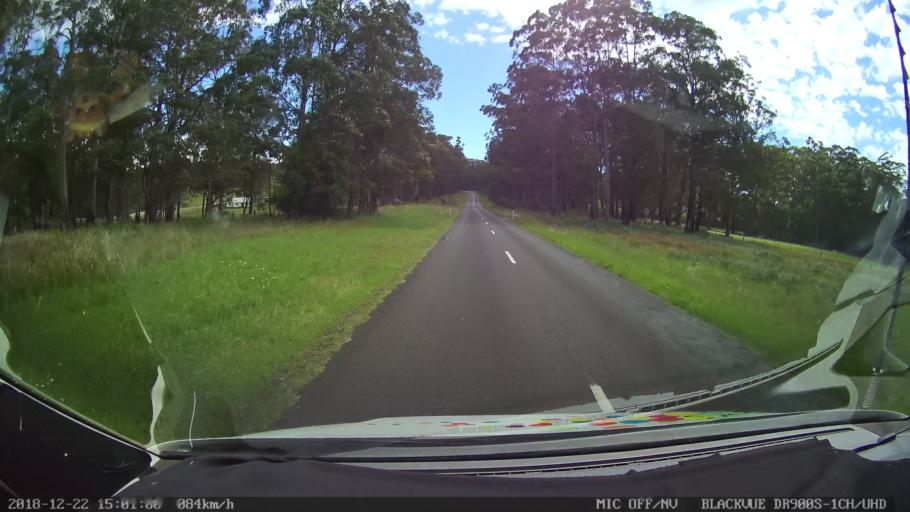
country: AU
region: New South Wales
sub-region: Bellingen
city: Dorrigo
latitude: -30.2502
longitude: 152.4626
